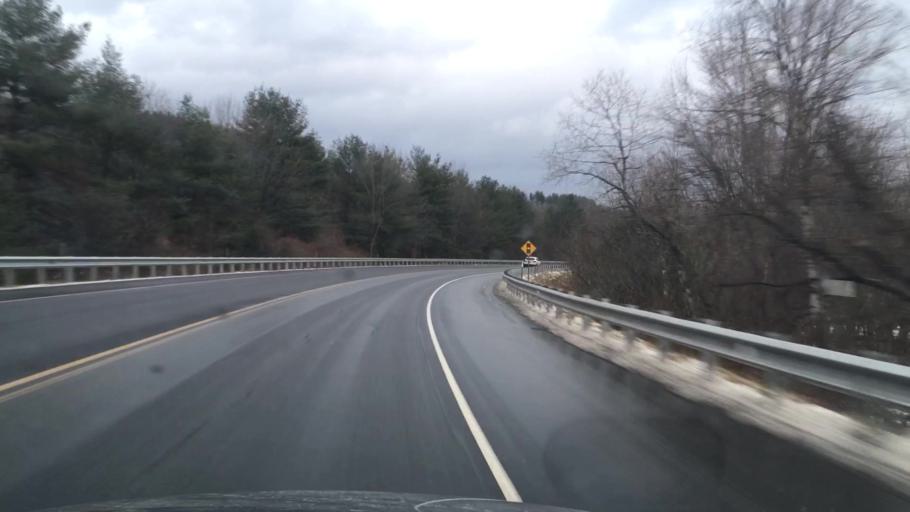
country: US
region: New Hampshire
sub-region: Sullivan County
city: Claremont
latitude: 43.4023
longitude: -72.3965
